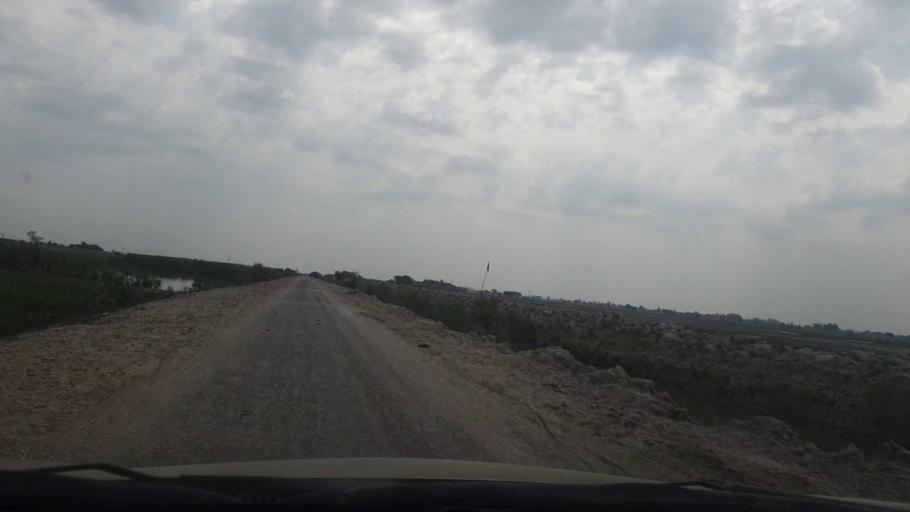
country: PK
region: Sindh
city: Ratodero
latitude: 27.6981
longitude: 68.2238
